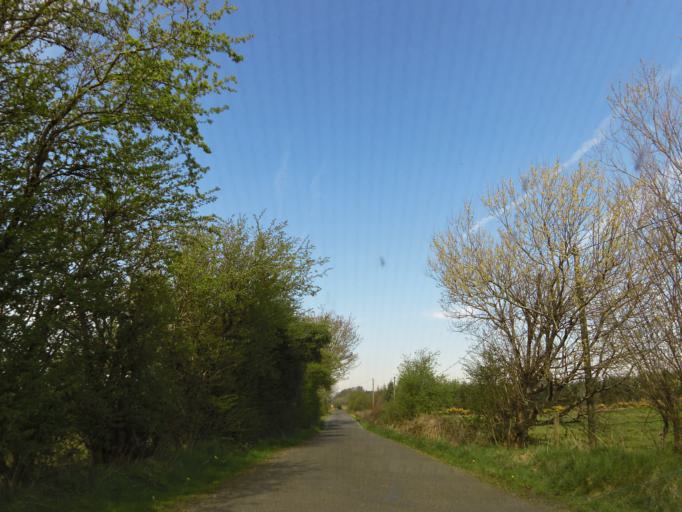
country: IE
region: Connaught
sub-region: Maigh Eo
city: Kiltamagh
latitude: 53.8238
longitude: -8.9899
